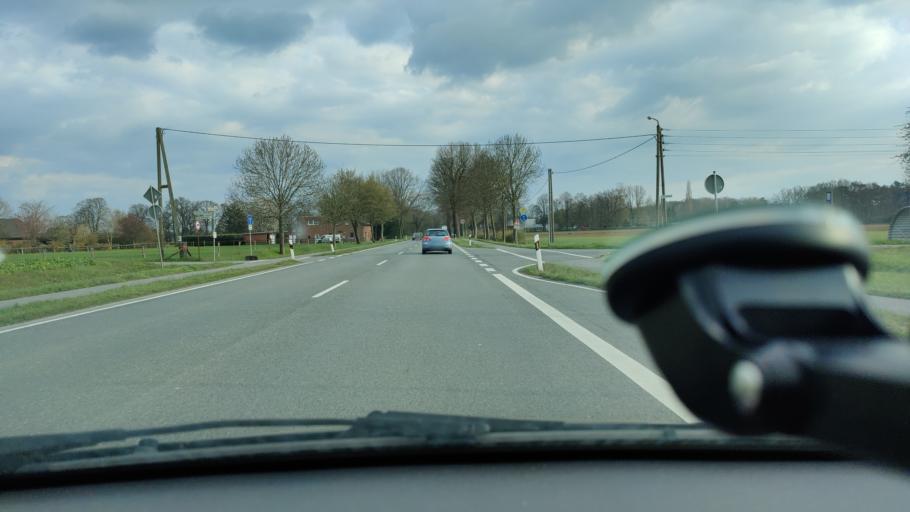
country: DE
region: North Rhine-Westphalia
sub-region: Regierungsbezirk Dusseldorf
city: Hamminkeln
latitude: 51.6998
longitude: 6.6036
